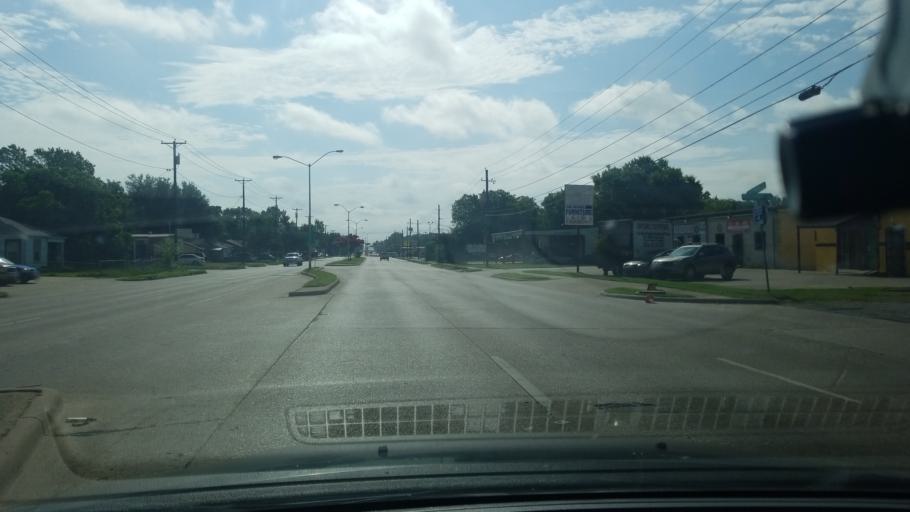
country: US
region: Texas
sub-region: Dallas County
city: Balch Springs
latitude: 32.7341
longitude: -96.6691
